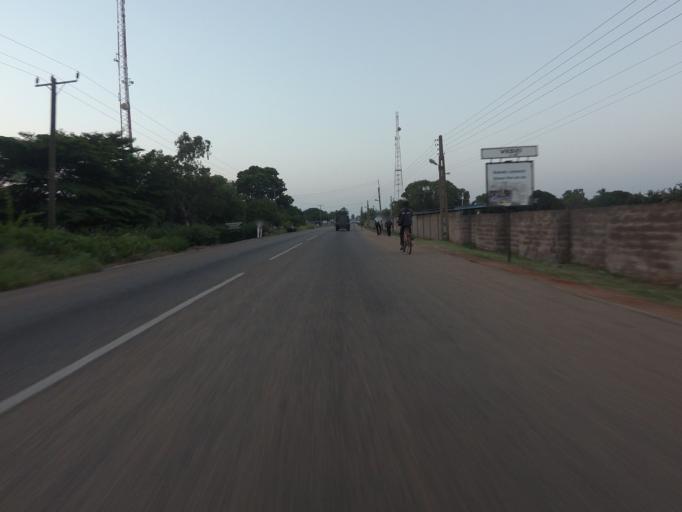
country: GH
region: Volta
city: Keta
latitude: 5.8964
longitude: 0.9872
